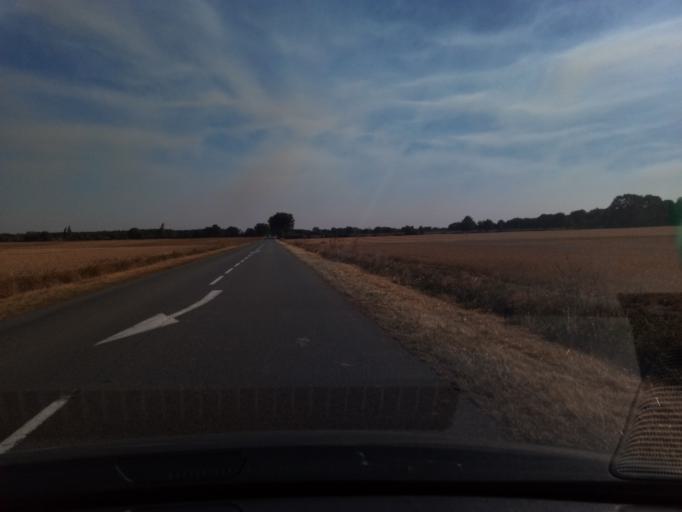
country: FR
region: Poitou-Charentes
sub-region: Departement de la Vienne
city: Montmorillon
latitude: 46.4936
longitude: 0.7831
